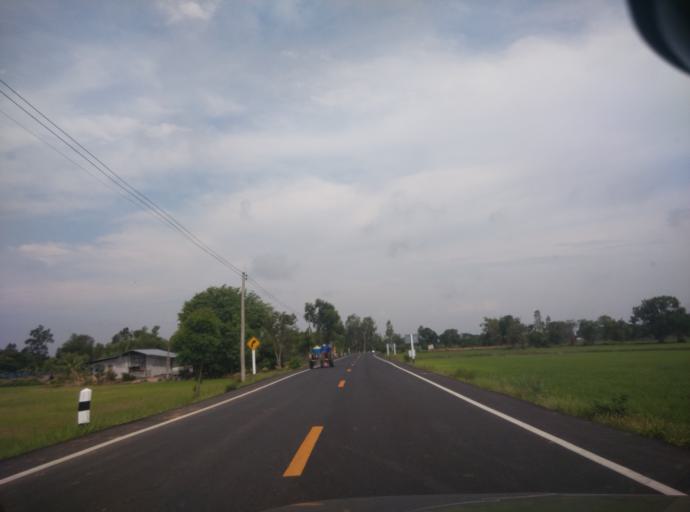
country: TH
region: Sisaket
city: Uthumphon Phisai
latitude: 15.1196
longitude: 104.2213
